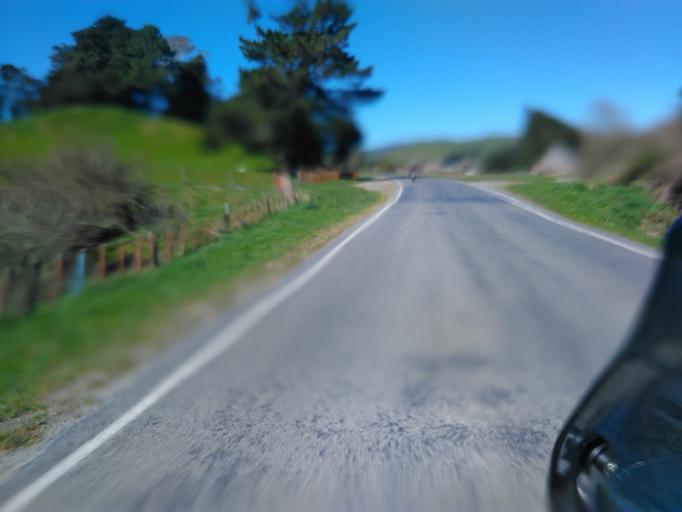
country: NZ
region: Bay of Plenty
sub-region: Opotiki District
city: Opotiki
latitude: -38.3470
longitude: 177.5324
